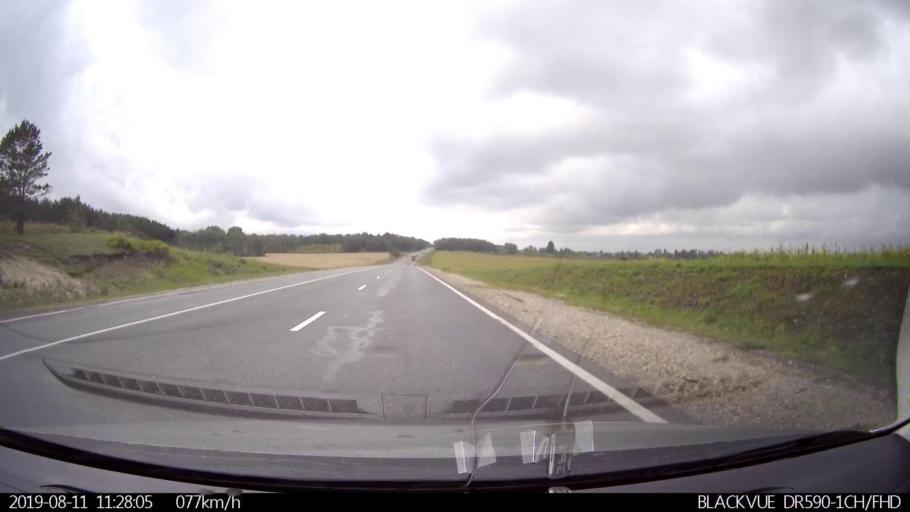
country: RU
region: Ulyanovsk
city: Krasnyy Gulyay
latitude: 54.0846
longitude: 48.2286
